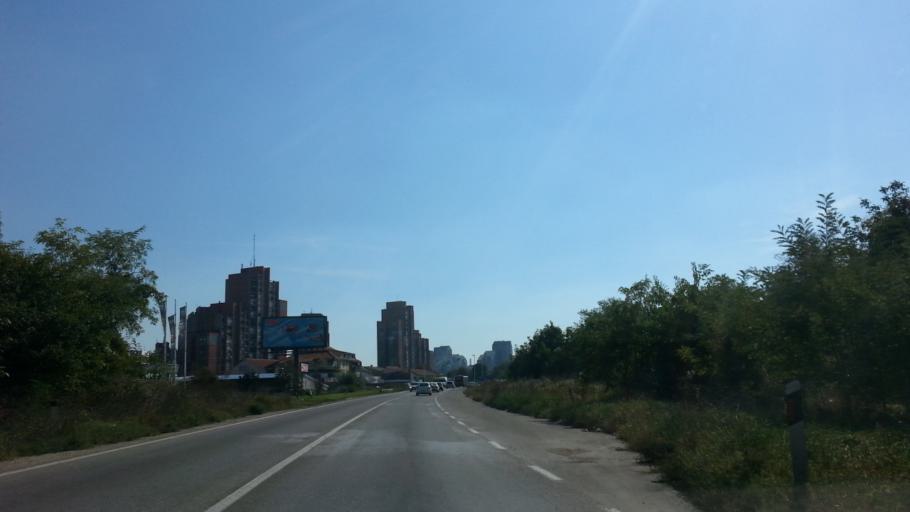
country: RS
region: Central Serbia
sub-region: Belgrade
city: Rakovica
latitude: 44.7372
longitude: 20.4181
